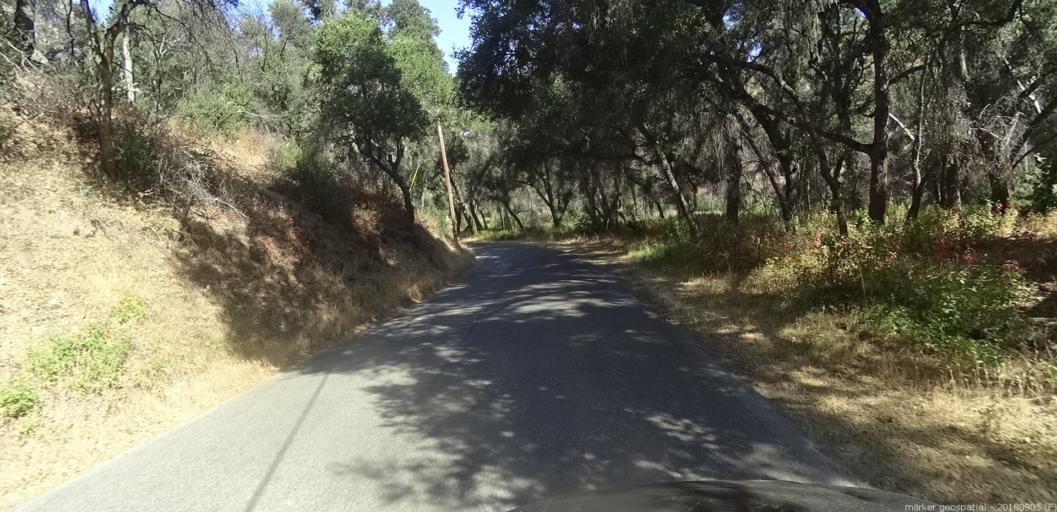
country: US
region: California
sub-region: Monterey County
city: Gonzales
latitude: 36.3825
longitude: -121.5935
